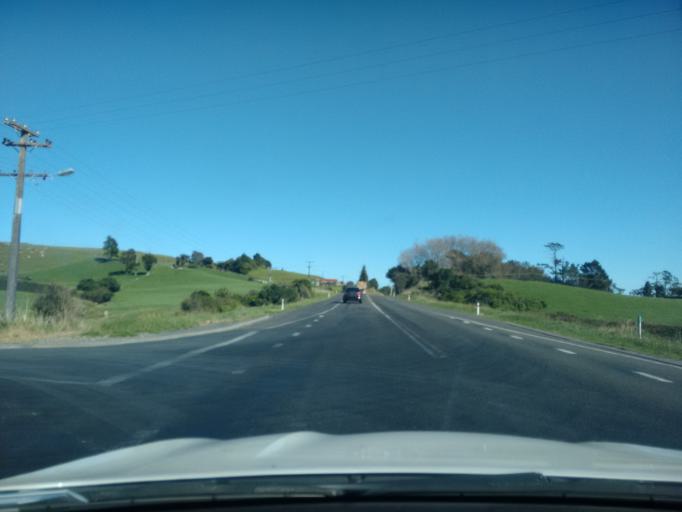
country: NZ
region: Taranaki
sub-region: New Plymouth District
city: New Plymouth
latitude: -39.1514
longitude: 174.1601
